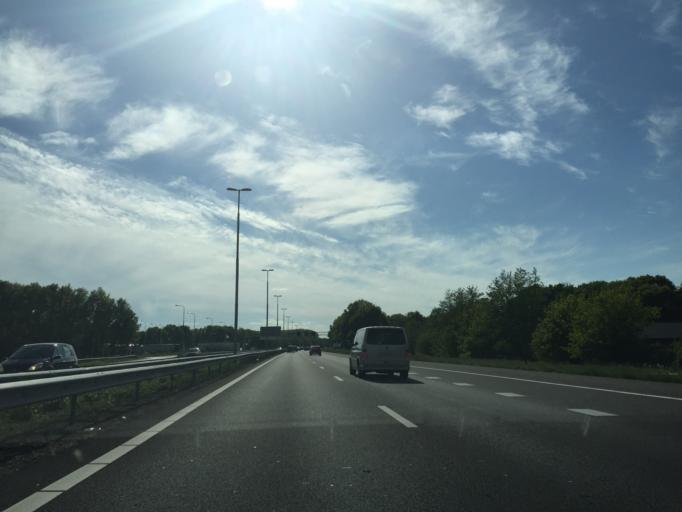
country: NL
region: Gelderland
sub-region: Gemeente Barneveld
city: Terschuur
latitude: 52.1642
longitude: 5.5385
